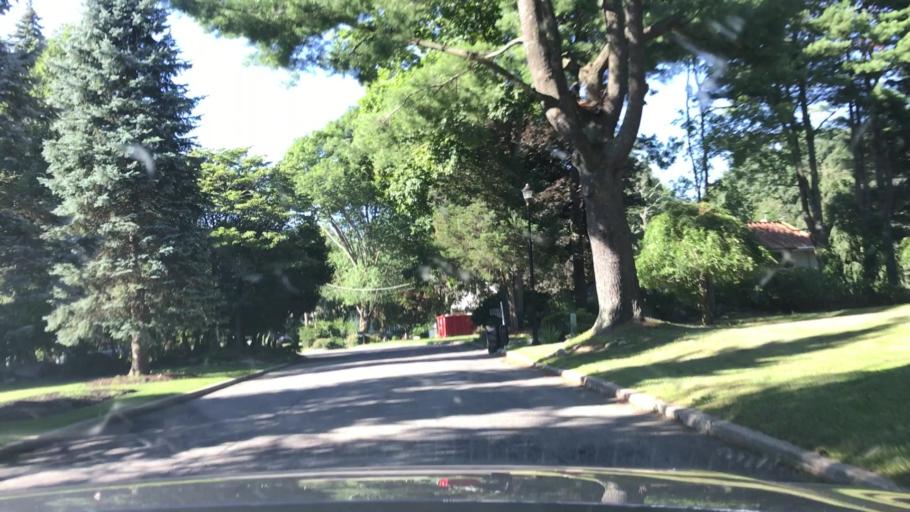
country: US
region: New York
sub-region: Westchester County
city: Thornwood
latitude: 41.1090
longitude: -73.7791
